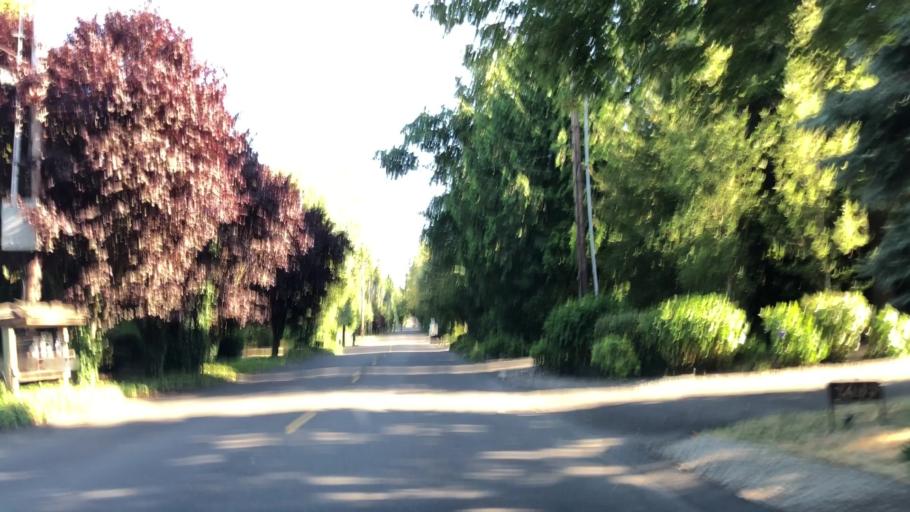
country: US
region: Washington
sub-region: King County
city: Medina
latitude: 47.6353
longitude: -122.2386
